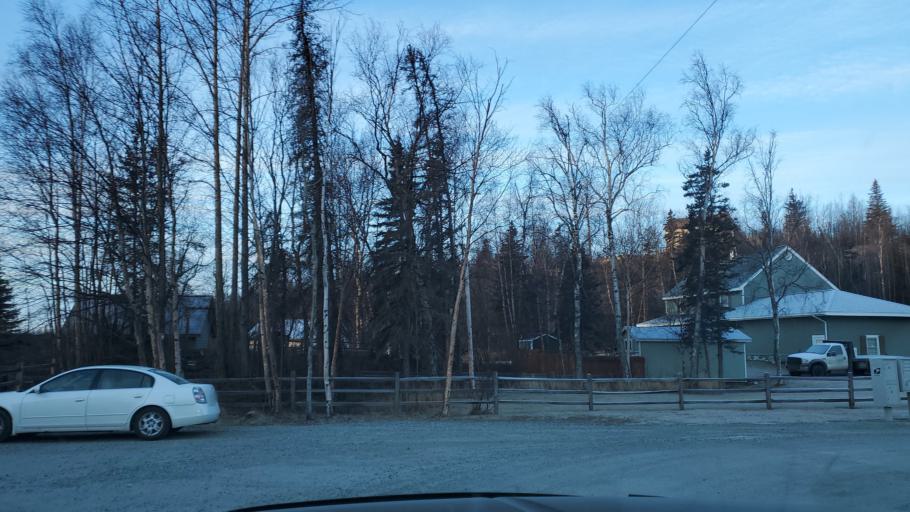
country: US
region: Alaska
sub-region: Matanuska-Susitna Borough
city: Lakes
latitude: 61.6006
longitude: -149.3162
